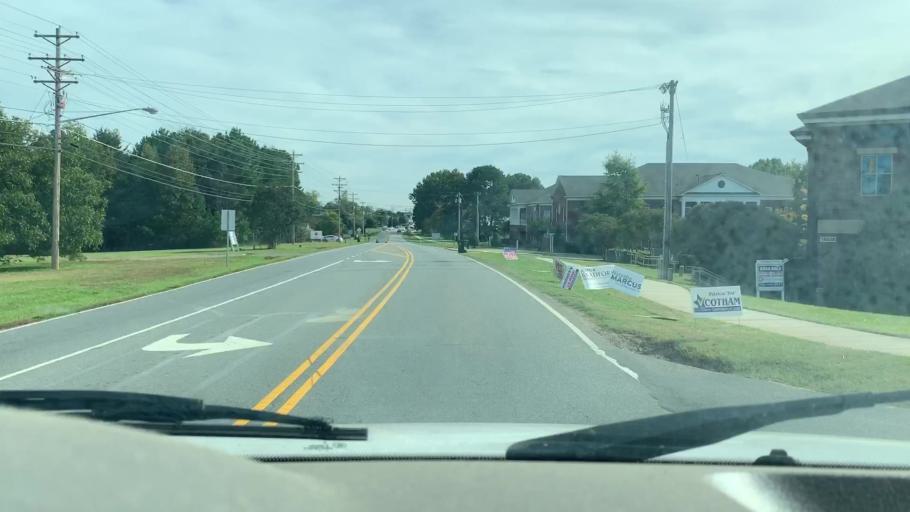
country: US
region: North Carolina
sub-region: Mecklenburg County
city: Cornelius
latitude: 35.4707
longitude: -80.8914
